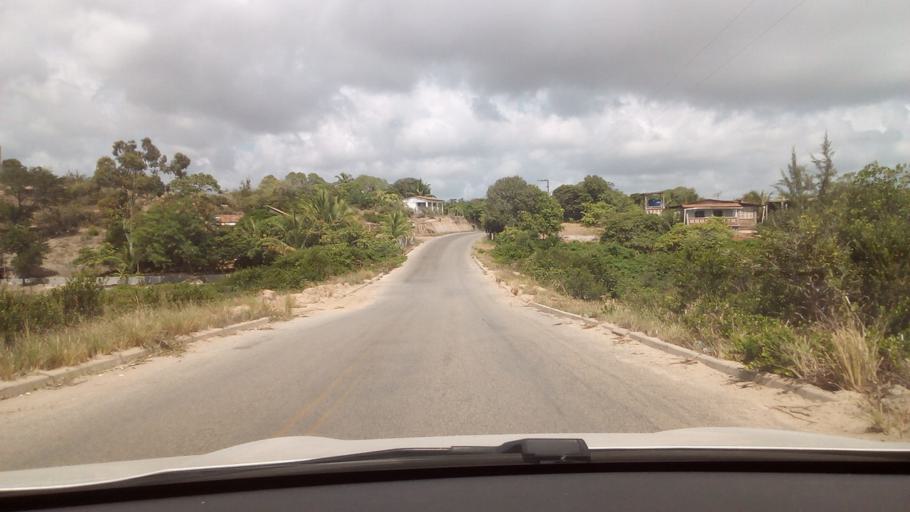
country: BR
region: Paraiba
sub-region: Conde
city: Conde
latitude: -7.3138
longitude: -34.8079
